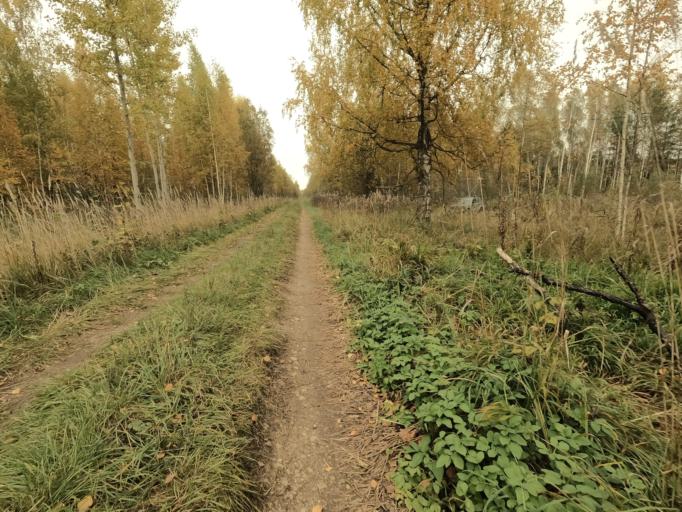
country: RU
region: Novgorod
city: Pankovka
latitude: 58.8784
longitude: 30.9417
